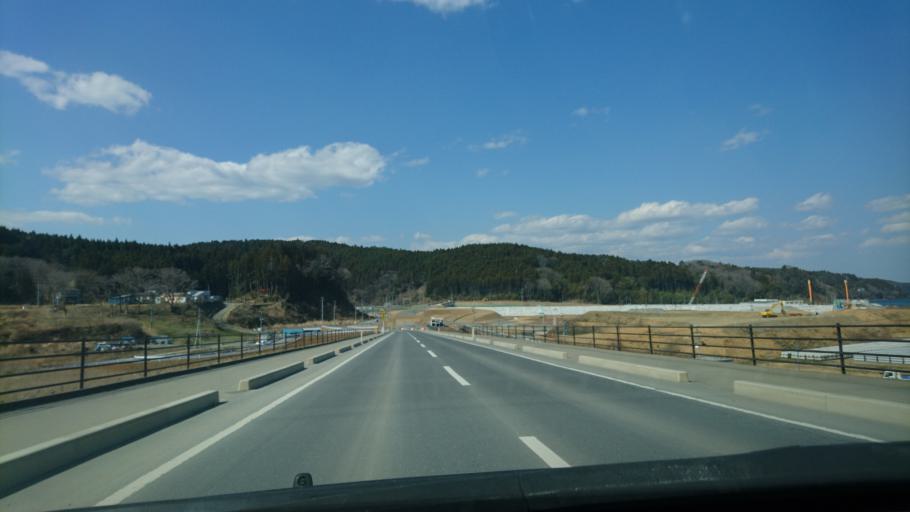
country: JP
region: Miyagi
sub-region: Oshika Gun
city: Onagawa Cho
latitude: 38.6423
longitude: 141.4386
